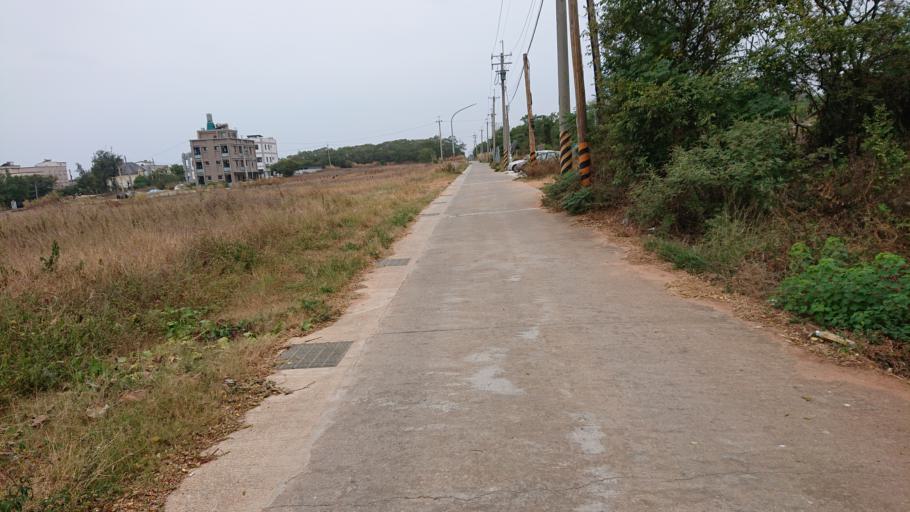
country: TW
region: Fukien
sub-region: Kinmen
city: Jincheng
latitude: 24.4465
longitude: 118.3129
